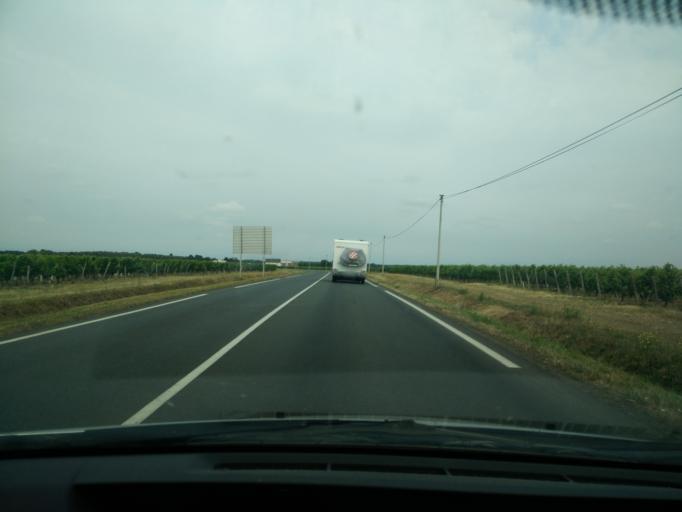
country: FR
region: Pays de la Loire
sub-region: Departement de Maine-et-Loire
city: Montreuil-Bellay
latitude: 47.1411
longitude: -0.1606
